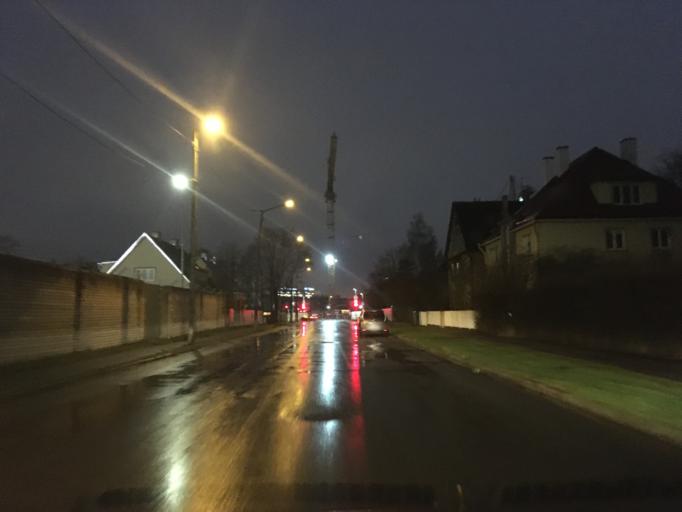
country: EE
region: Harju
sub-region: Tallinna linn
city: Tallinn
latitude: 59.4209
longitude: 24.7530
